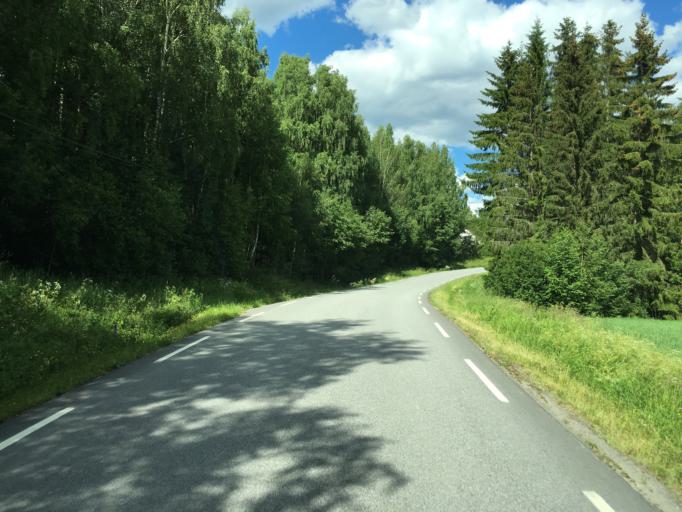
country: NO
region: Oppland
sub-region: Sondre Land
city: Hov
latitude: 60.6172
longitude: 10.3360
